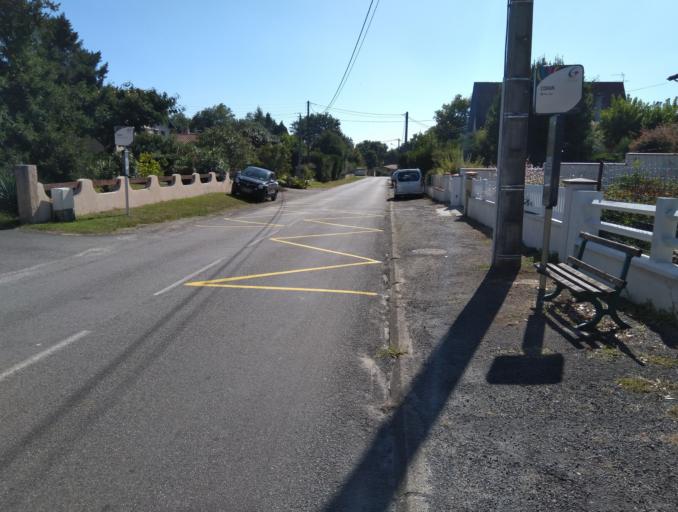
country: FR
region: Aquitaine
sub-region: Departement des Landes
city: Saugnac-et-Cambran
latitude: 43.6786
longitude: -0.9892
